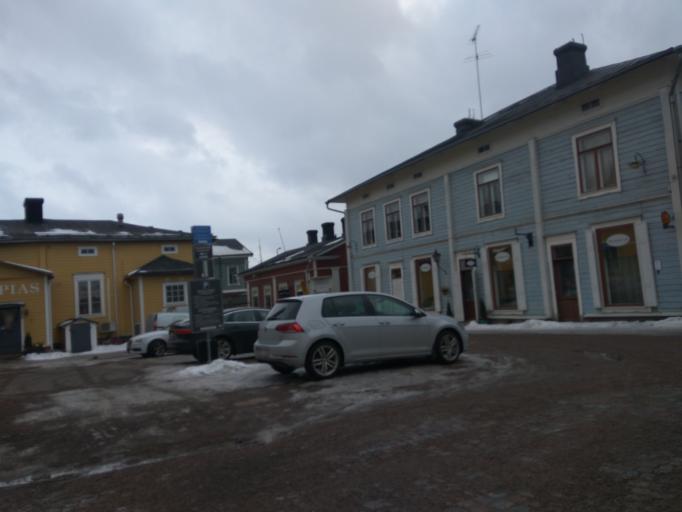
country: FI
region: Uusimaa
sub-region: Porvoo
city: Porvoo
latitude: 60.3943
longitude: 25.6589
